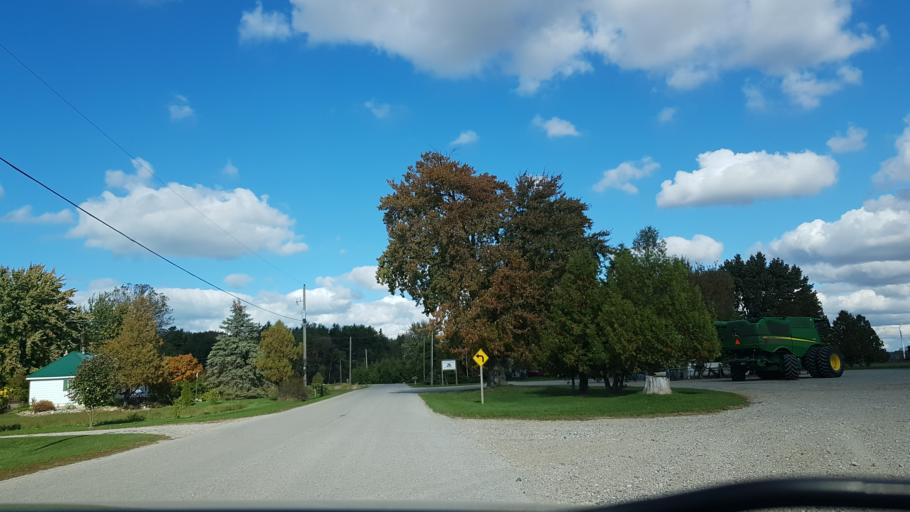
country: CA
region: Ontario
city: Lambton Shores
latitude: 43.2336
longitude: -81.7909
